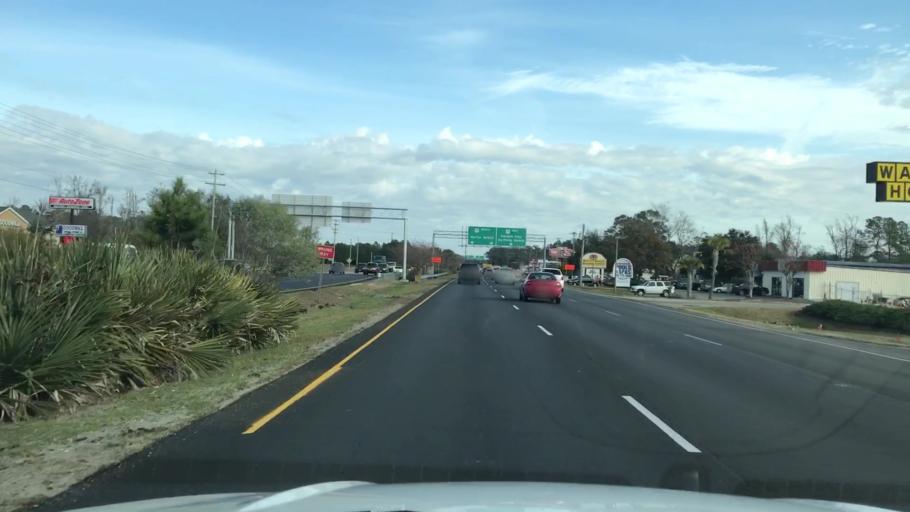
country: US
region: South Carolina
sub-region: Georgetown County
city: Murrells Inlet
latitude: 33.5675
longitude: -79.0343
